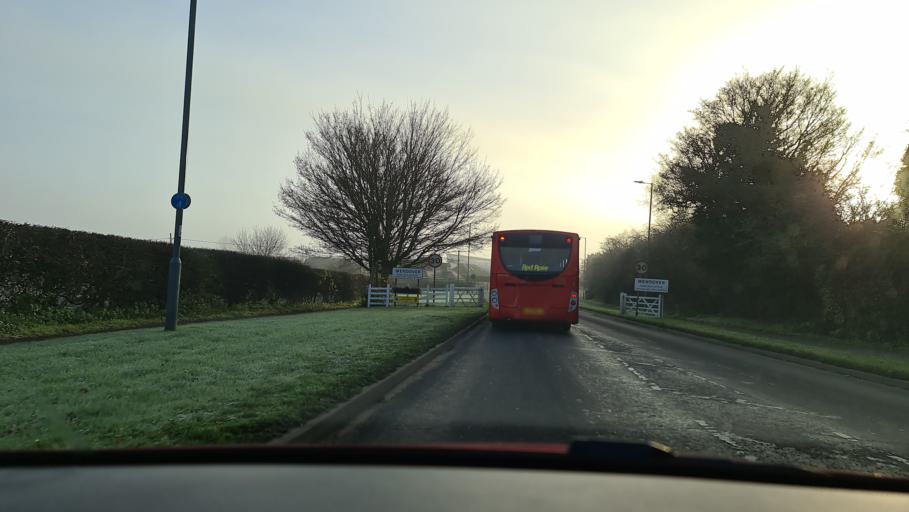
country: GB
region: England
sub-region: Buckinghamshire
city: Wendover
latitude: 51.7740
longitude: -0.7532
